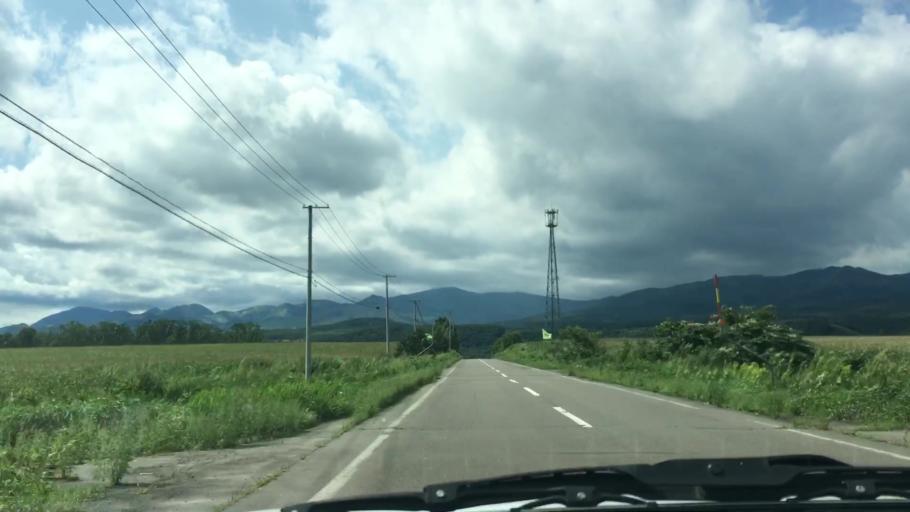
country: JP
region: Hokkaido
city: Otofuke
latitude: 43.2834
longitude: 143.3140
